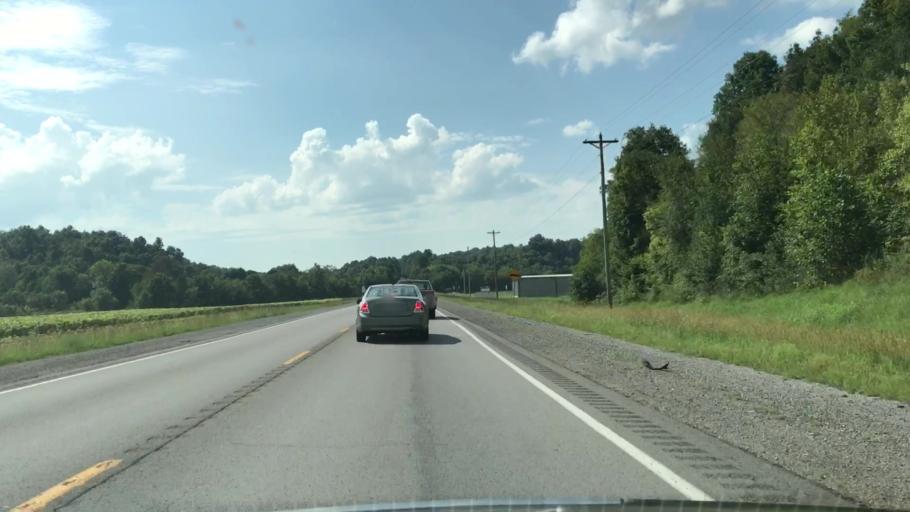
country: US
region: Kentucky
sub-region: Allen County
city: Scottsville
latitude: 36.6750
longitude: -86.2507
